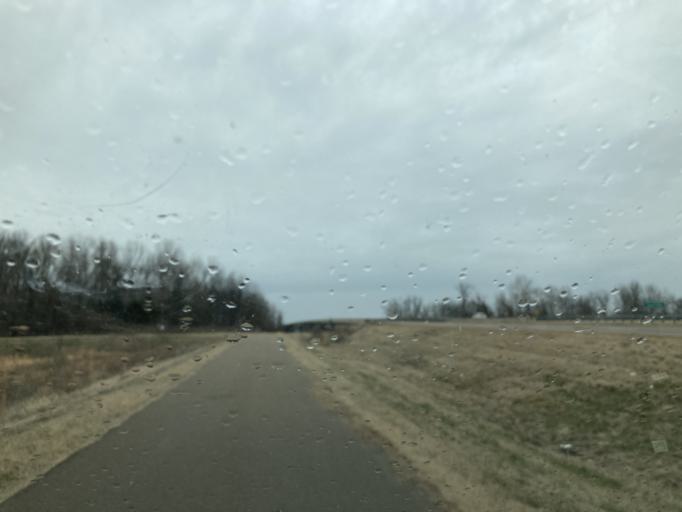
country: US
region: Mississippi
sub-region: Humphreys County
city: Belzoni
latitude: 33.0514
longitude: -90.4683
